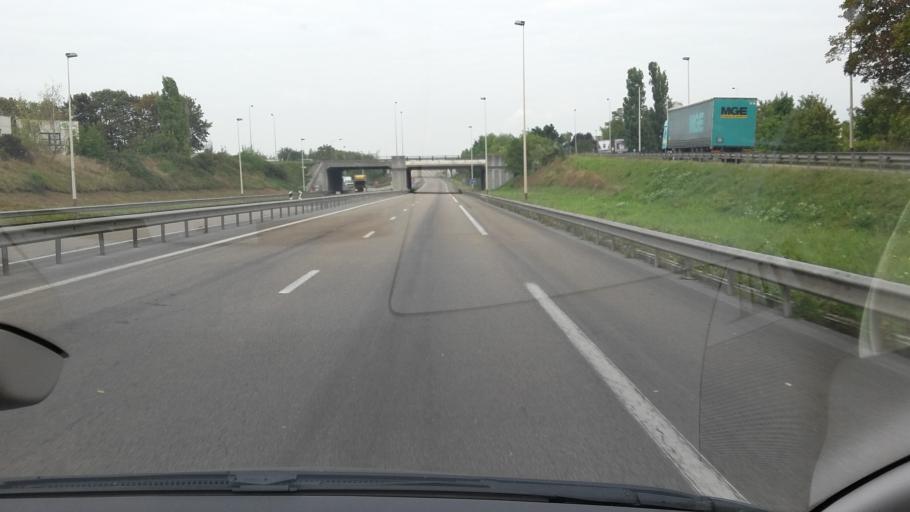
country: FR
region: Champagne-Ardenne
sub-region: Departement de la Marne
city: Taissy
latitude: 49.2337
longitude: 4.0738
